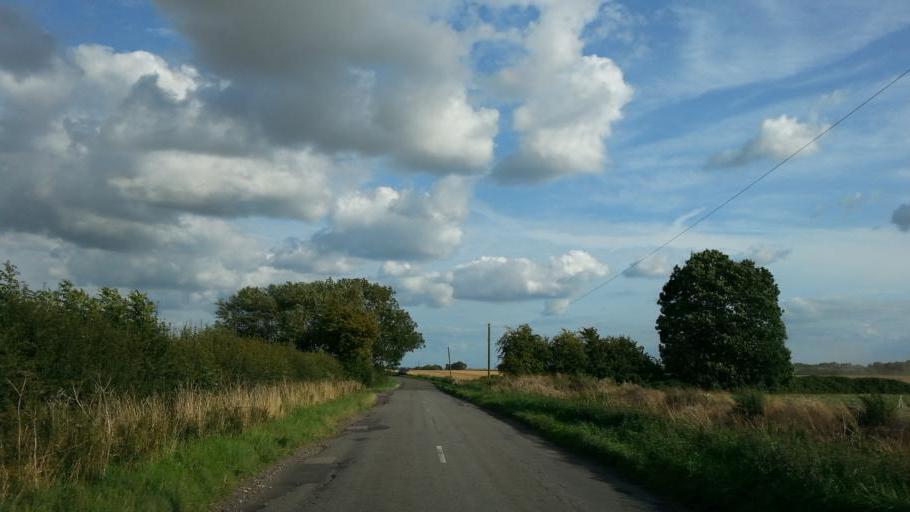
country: GB
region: England
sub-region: Nottinghamshire
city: Farndon
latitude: 53.0100
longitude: -0.8498
